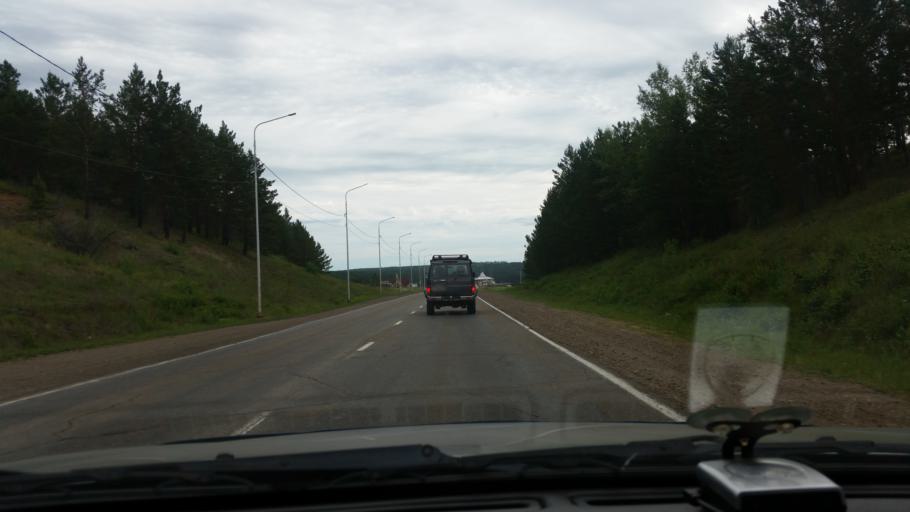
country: RU
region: Irkutsk
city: Oyek
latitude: 52.6525
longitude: 104.5316
